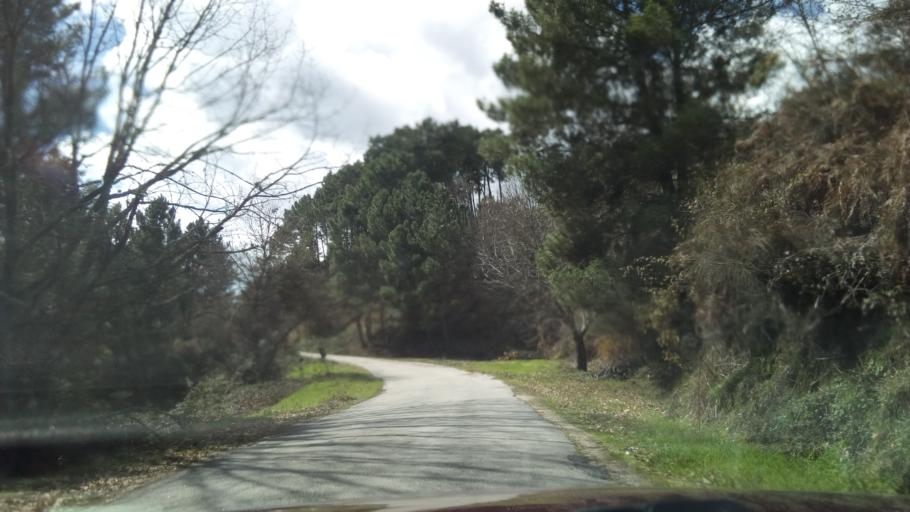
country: PT
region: Guarda
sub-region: Fornos de Algodres
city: Fornos de Algodres
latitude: 40.6590
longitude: -7.5032
